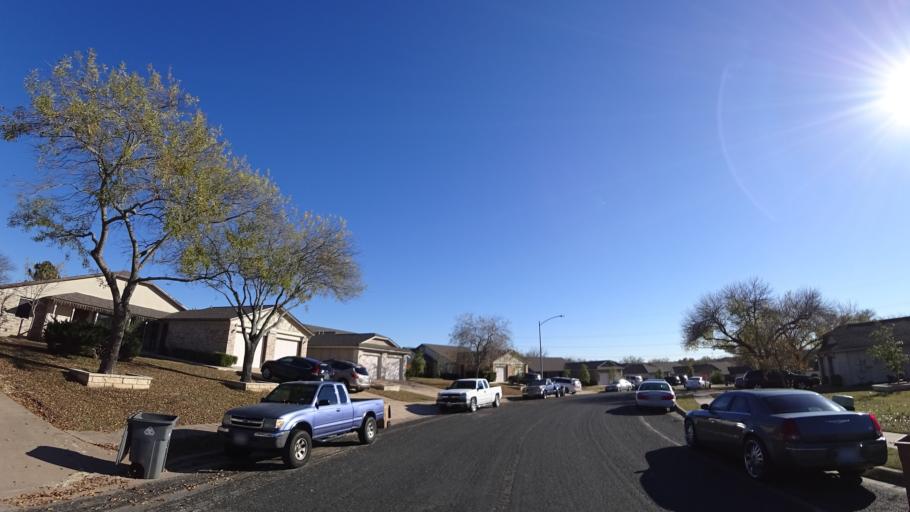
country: US
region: Texas
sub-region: Travis County
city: Wells Branch
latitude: 30.4081
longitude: -97.6951
